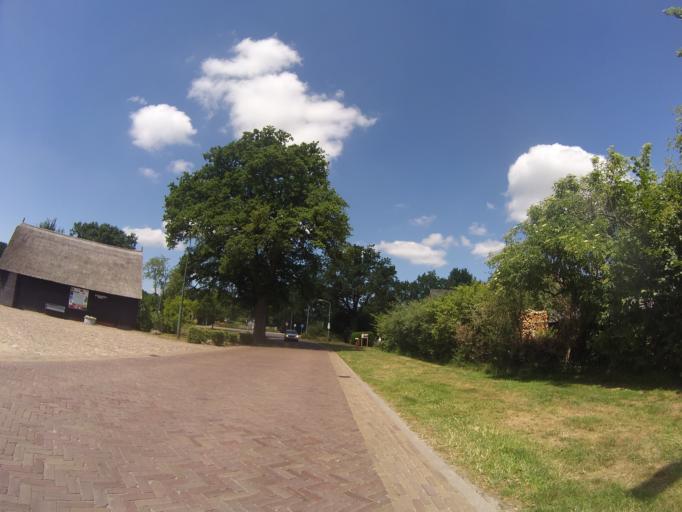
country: NL
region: Drenthe
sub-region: Gemeente Emmen
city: Emmen
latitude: 52.8416
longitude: 6.8800
